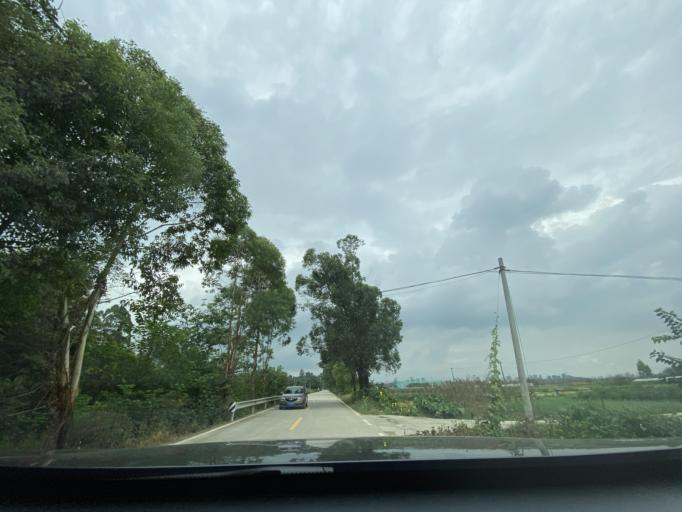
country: CN
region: Sichuan
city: Wujin
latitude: 30.3870
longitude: 103.9673
